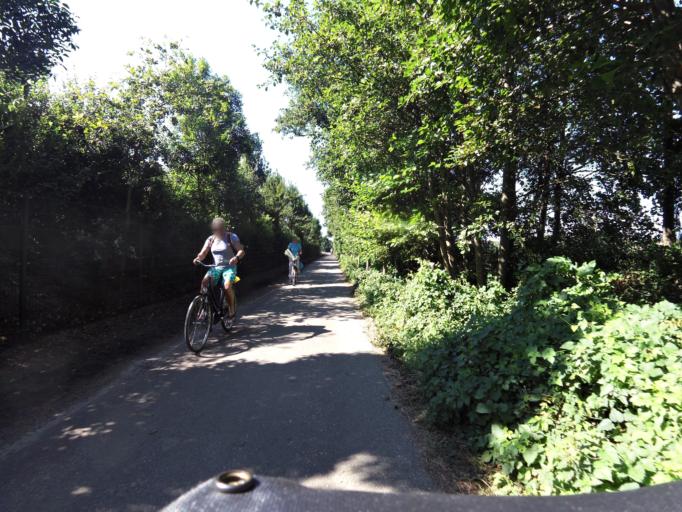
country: NL
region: Zeeland
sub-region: Schouwen-Duiveland
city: Renesse
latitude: 51.7333
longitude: 3.7552
